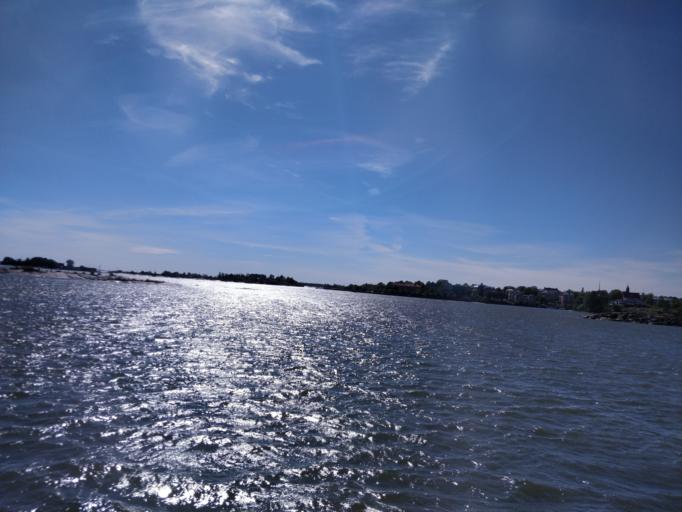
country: FI
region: Uusimaa
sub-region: Helsinki
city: Helsinki
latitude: 60.1595
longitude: 24.9783
